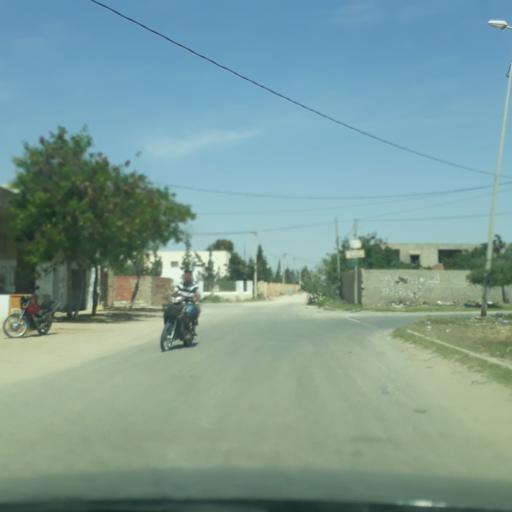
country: TN
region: Safaqis
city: Al Qarmadah
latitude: 34.8285
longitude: 10.7815
